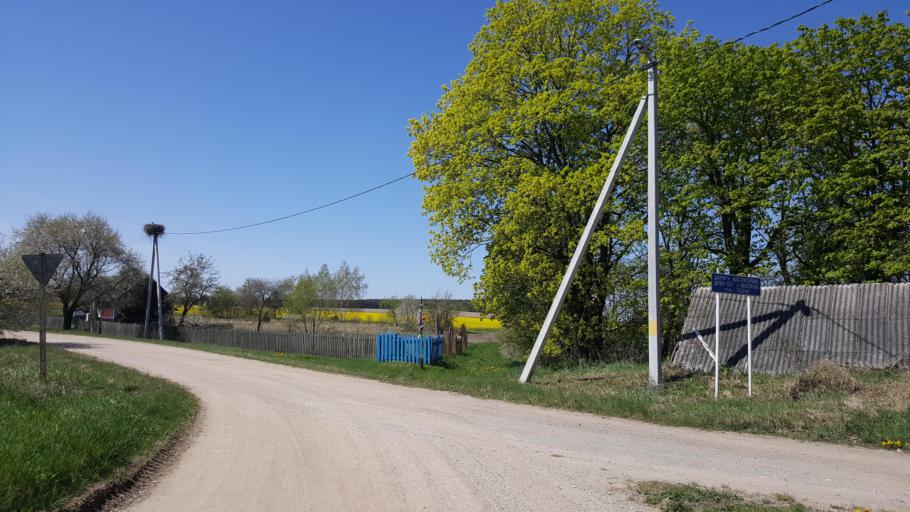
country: BY
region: Brest
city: Charnawchytsy
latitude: 52.3217
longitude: 23.7044
